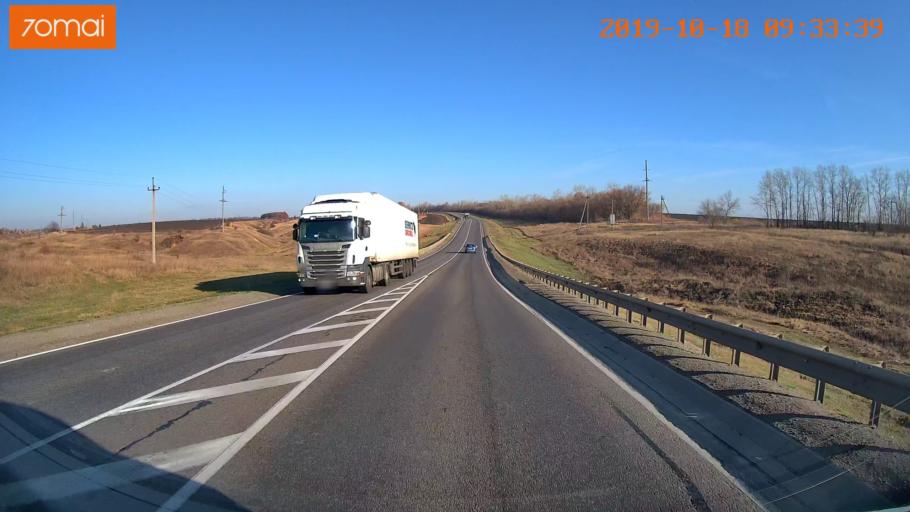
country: RU
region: Tula
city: Yefremov
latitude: 53.1695
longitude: 38.1516
